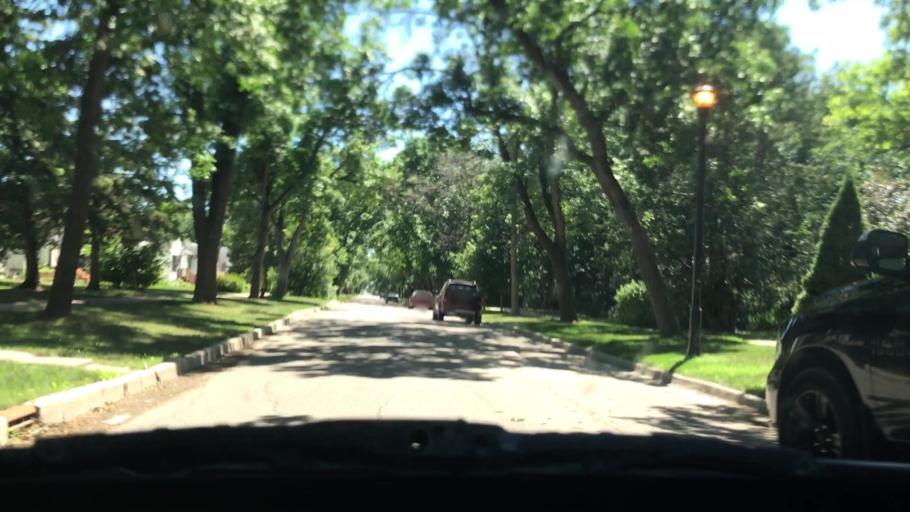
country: CA
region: Manitoba
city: Winnipeg
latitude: 49.8730
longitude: -97.1957
